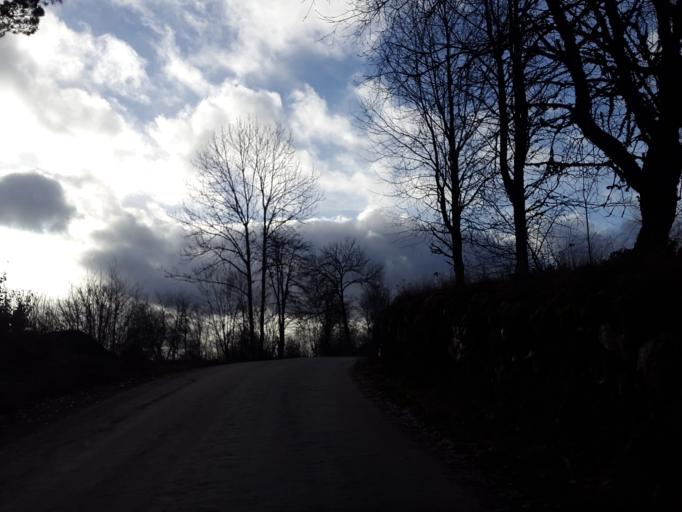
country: SE
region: Vaestra Goetaland
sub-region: Vargarda Kommun
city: Jonstorp
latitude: 57.9700
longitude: 12.7359
